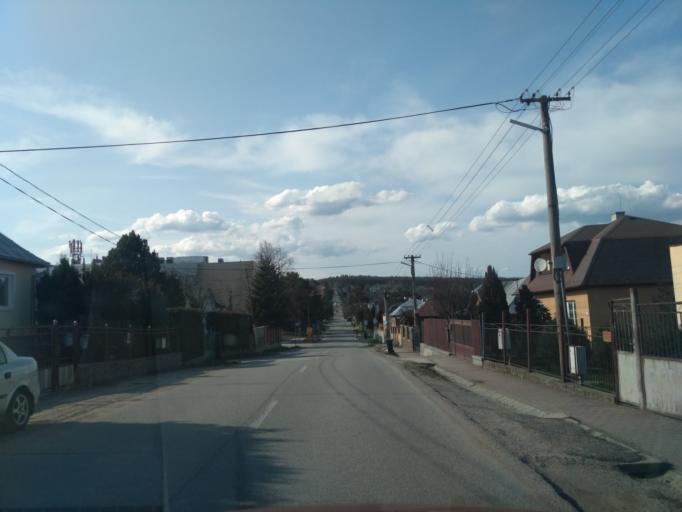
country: SK
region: Kosicky
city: Kosice
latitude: 48.6883
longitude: 21.2127
